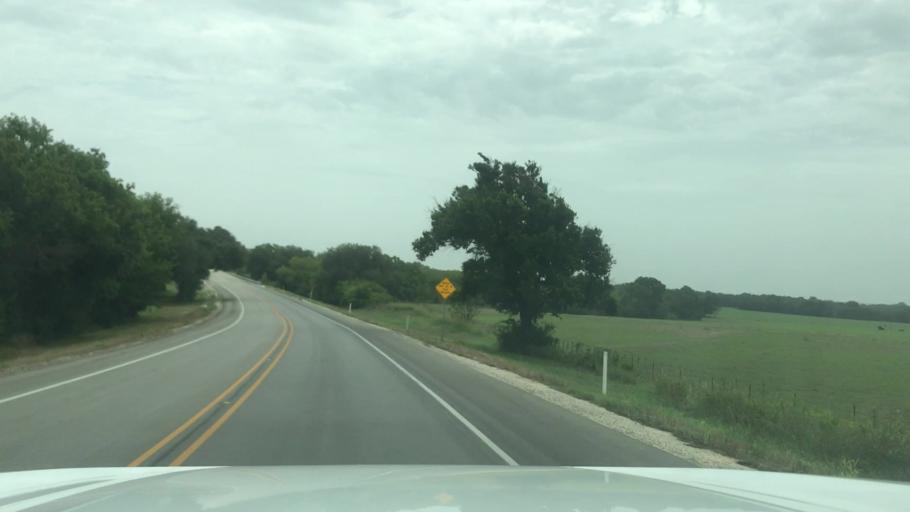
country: US
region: Texas
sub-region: Erath County
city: Dublin
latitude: 32.0748
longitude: -98.2329
